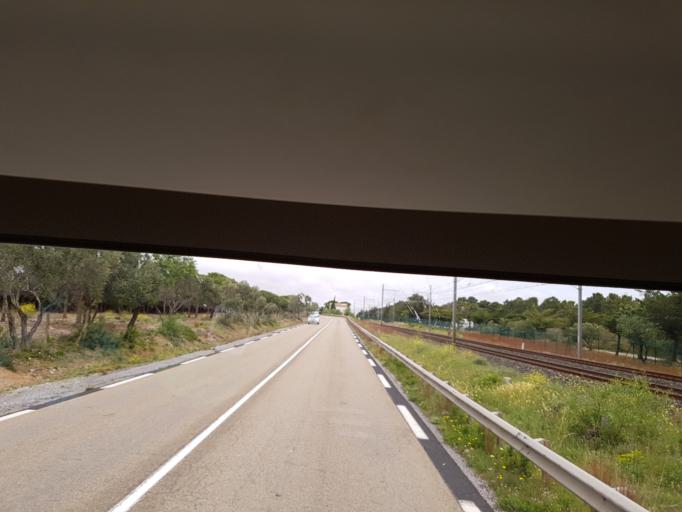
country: FR
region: Languedoc-Roussillon
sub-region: Departement de l'Aude
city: Leucate
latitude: 42.8758
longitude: 2.9928
